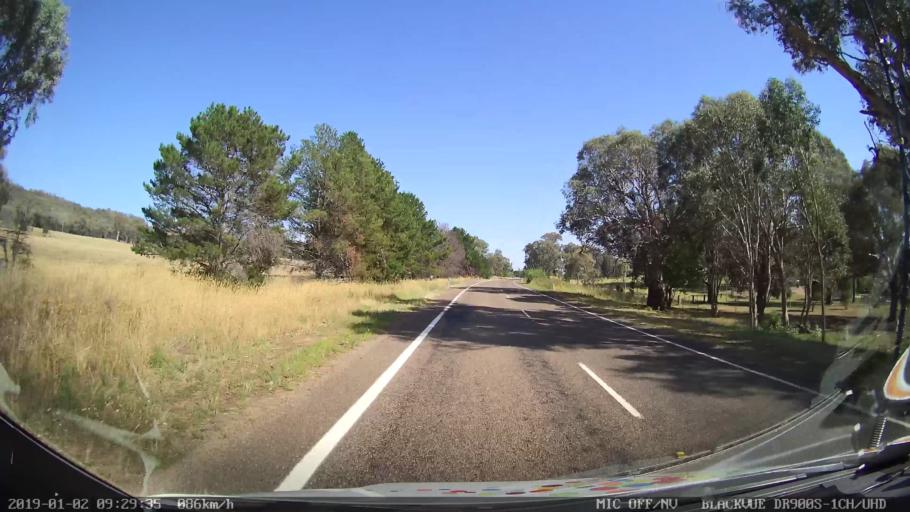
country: AU
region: New South Wales
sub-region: Tumut Shire
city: Tumut
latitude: -35.3371
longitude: 148.2411
